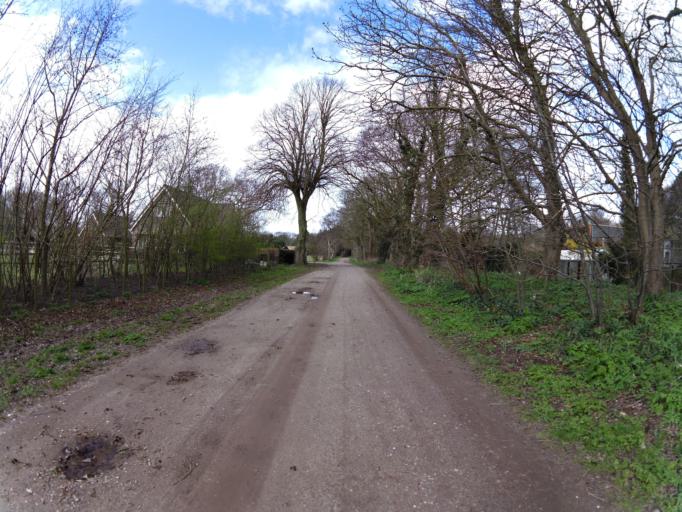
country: NL
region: South Holland
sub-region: Gemeente Hellevoetsluis
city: Nieuwenhoorn
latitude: 51.9049
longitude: 4.0827
